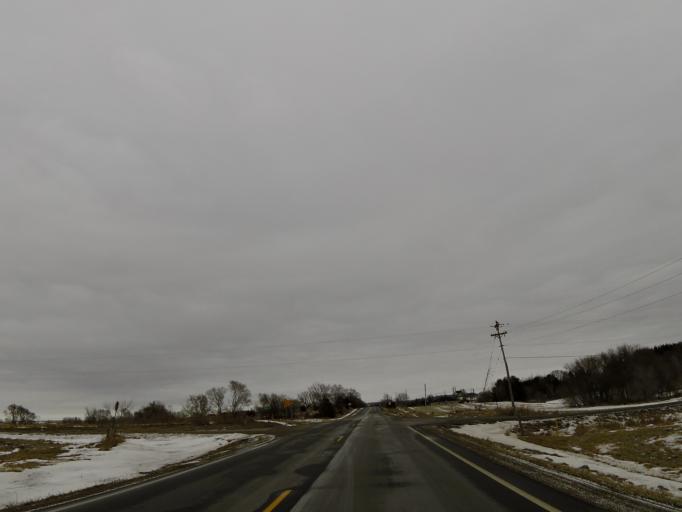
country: US
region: Minnesota
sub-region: Dakota County
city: Hastings
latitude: 44.7901
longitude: -92.8432
